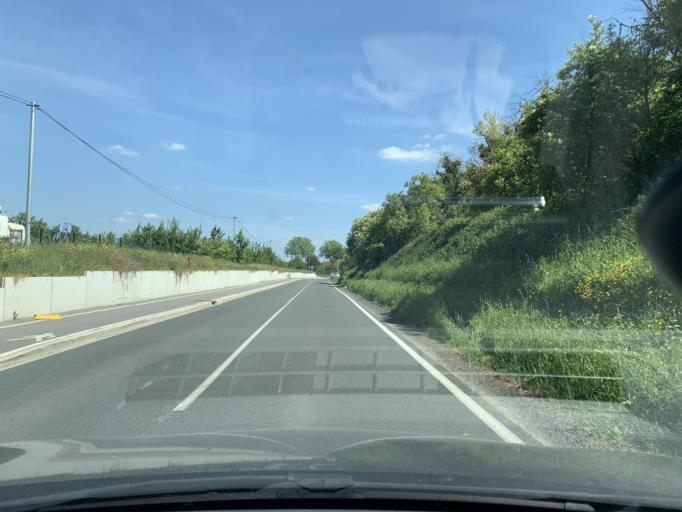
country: FR
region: Nord-Pas-de-Calais
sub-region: Departement du Nord
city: Caudry
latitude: 50.1082
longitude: 3.4193
